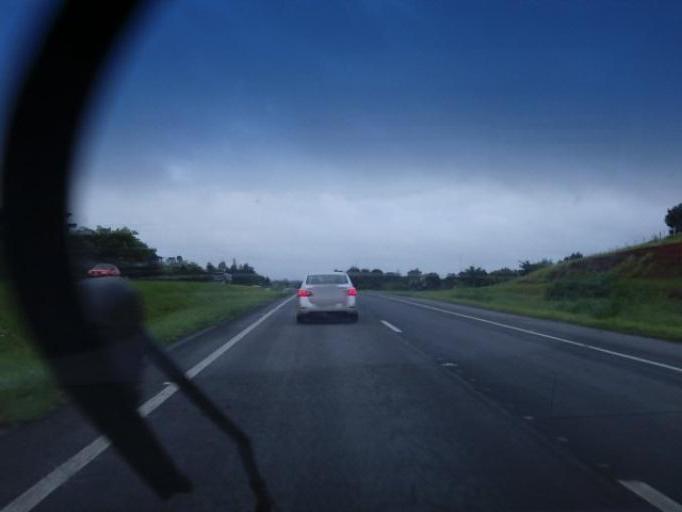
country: BR
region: Sao Paulo
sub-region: Registro
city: Registro
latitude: -24.4668
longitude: -47.8208
